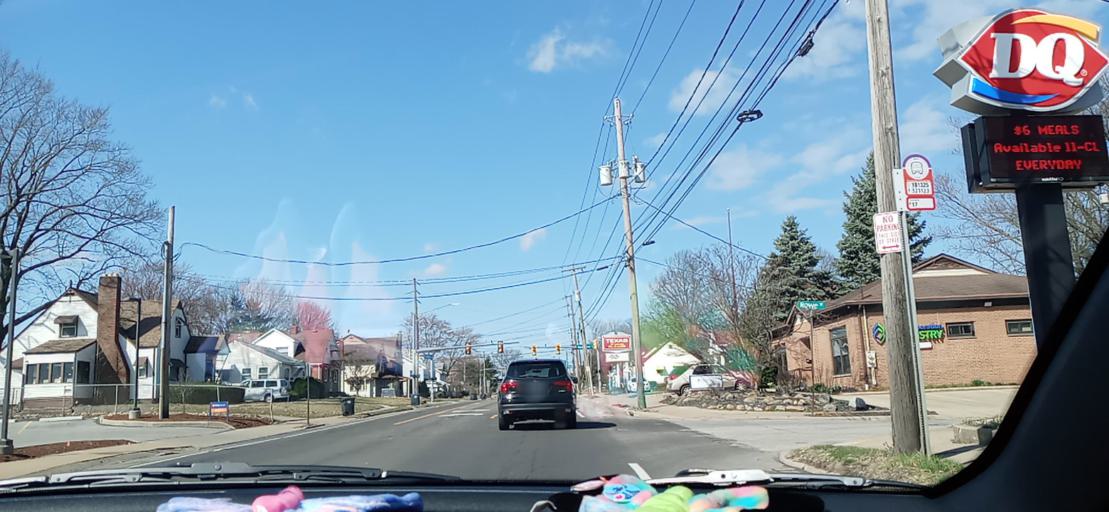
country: US
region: Ohio
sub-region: Summit County
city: Portage Lakes
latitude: 41.0399
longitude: -81.5019
